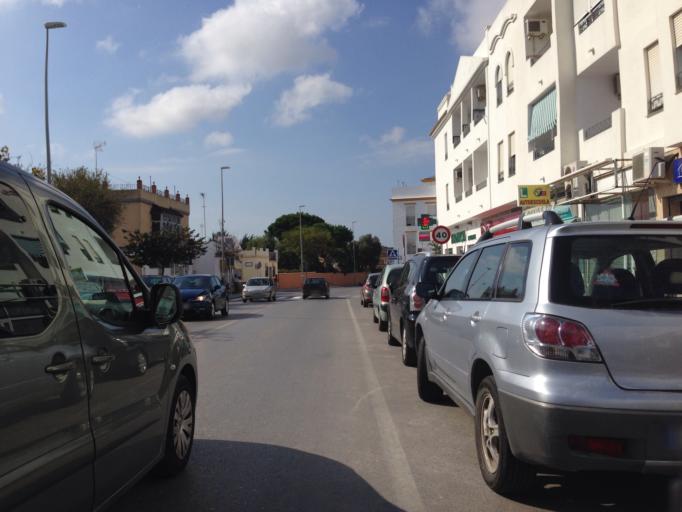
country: ES
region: Andalusia
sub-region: Provincia de Cadiz
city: Chiclana de la Frontera
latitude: 36.4176
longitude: -6.1577
